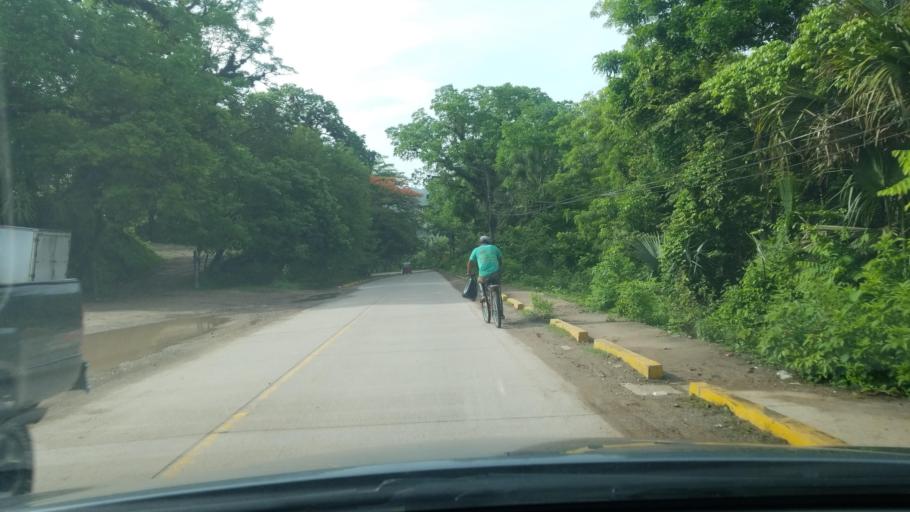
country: HN
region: Copan
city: Copan
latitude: 14.8401
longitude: -89.1522
